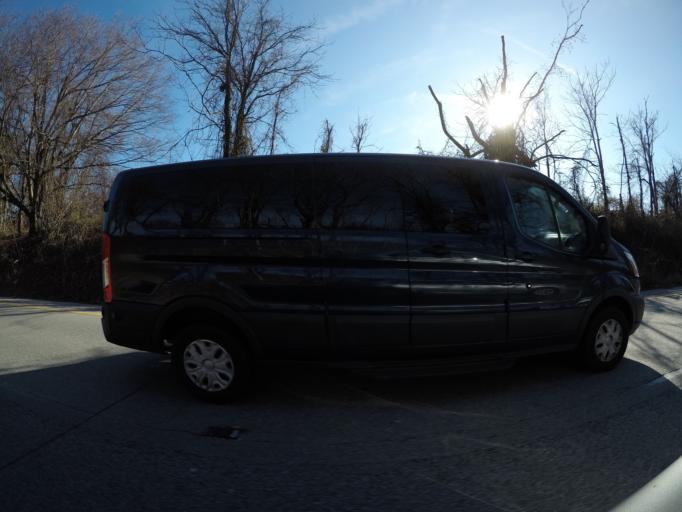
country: US
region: Pennsylvania
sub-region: Chester County
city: Parkesburg
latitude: 39.9842
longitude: -75.9152
